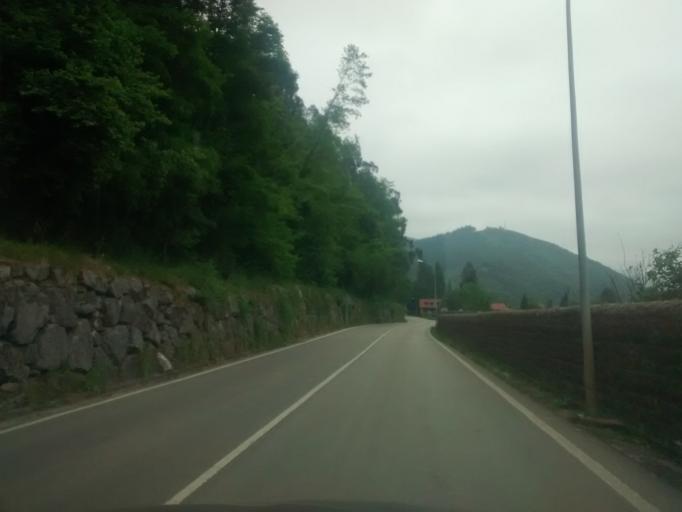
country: ES
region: Cantabria
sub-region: Provincia de Cantabria
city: Ruente
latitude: 43.2216
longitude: -4.3027
